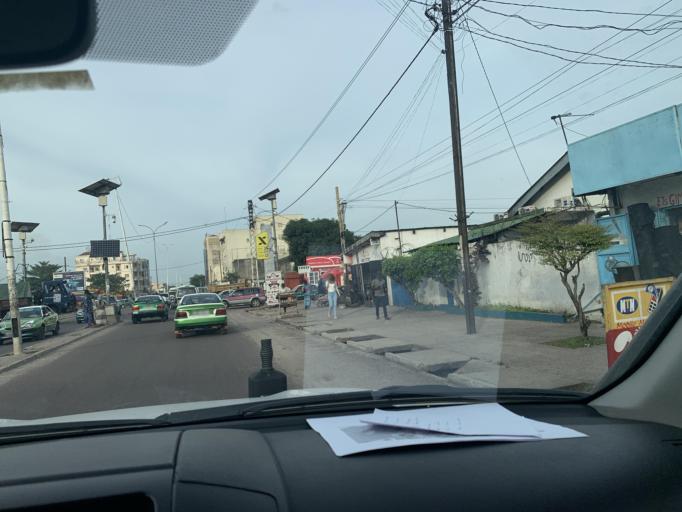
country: CG
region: Brazzaville
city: Brazzaville
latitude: -4.2491
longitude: 15.2800
